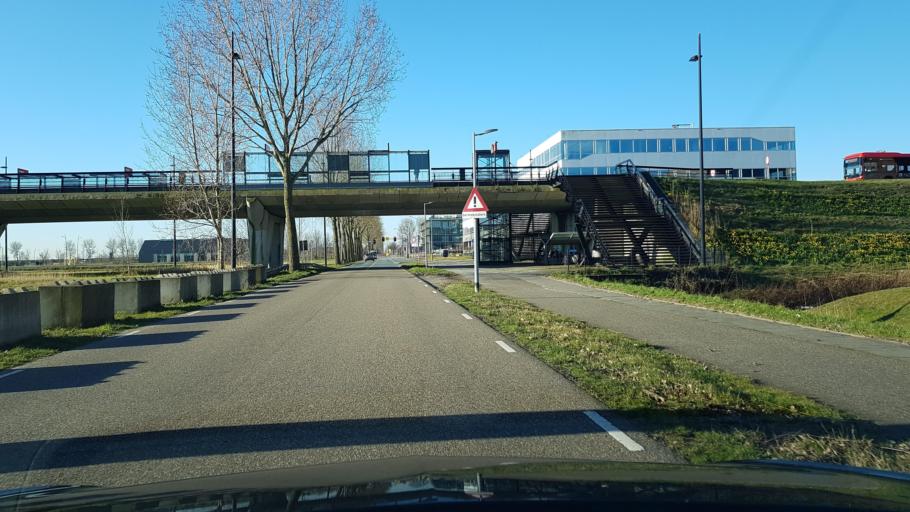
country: NL
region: North Holland
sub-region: Gemeente Haarlemmermeer
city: Hoofddorp
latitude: 52.2896
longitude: 4.7097
